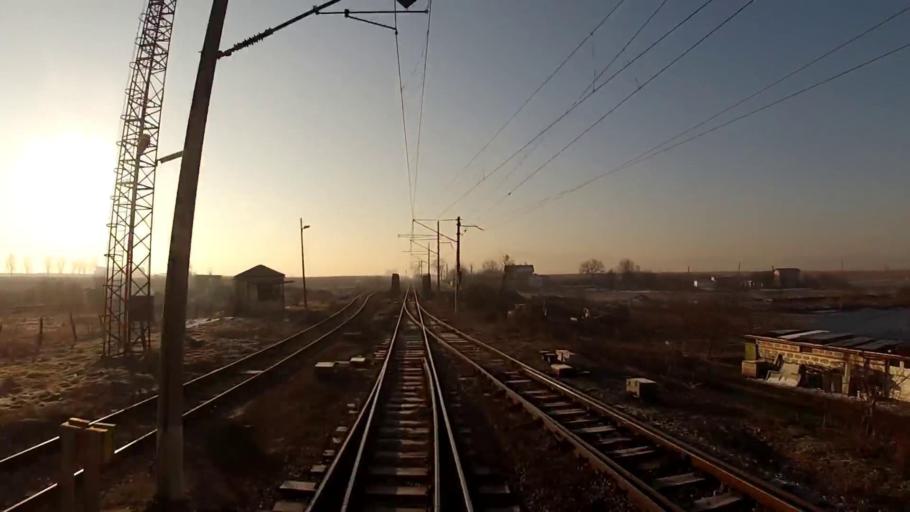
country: BG
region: Sofiya
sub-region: Obshtina Kostinbrod
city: Kostinbrod
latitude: 42.7974
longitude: 23.2064
